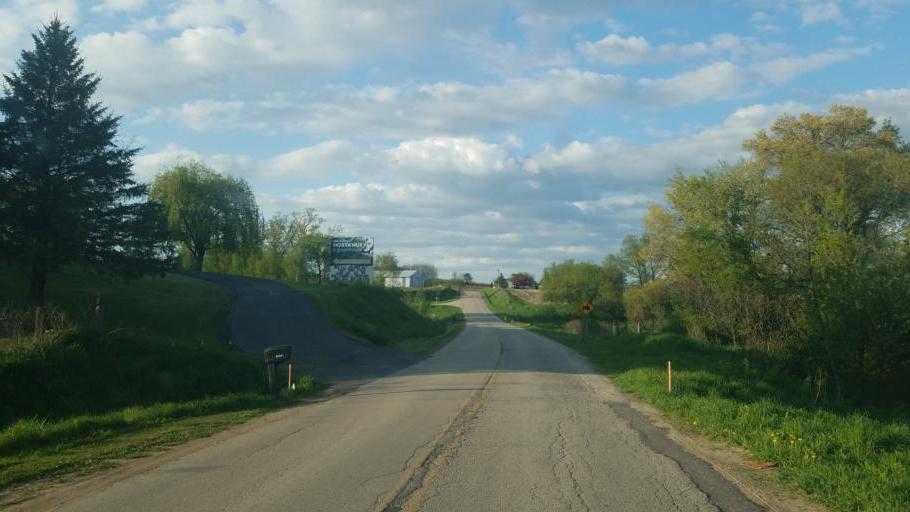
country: US
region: Wisconsin
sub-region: Vernon County
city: Hillsboro
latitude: 43.6601
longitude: -90.3313
